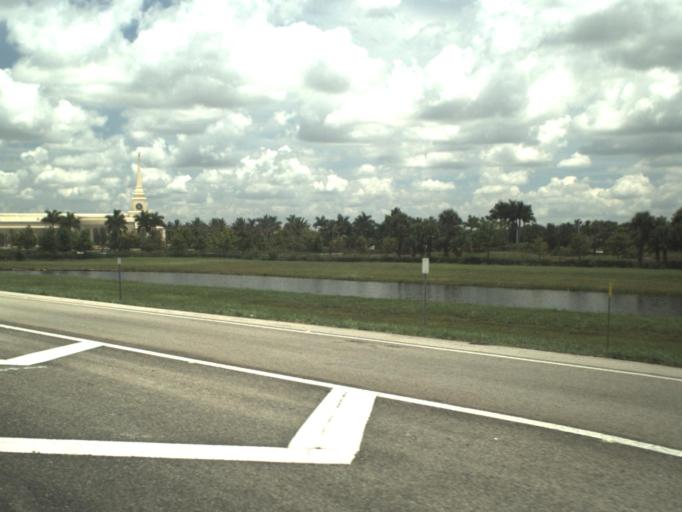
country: US
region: Florida
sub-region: Broward County
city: Southwest Ranches
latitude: 26.0676
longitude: -80.3556
